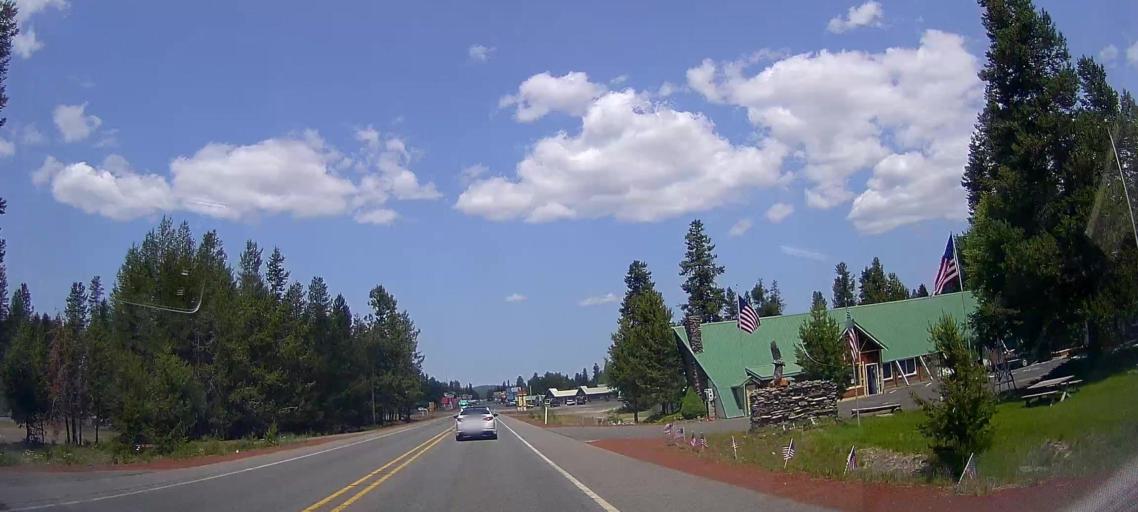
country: US
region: Oregon
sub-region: Deschutes County
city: La Pine
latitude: 43.2114
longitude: -121.7807
